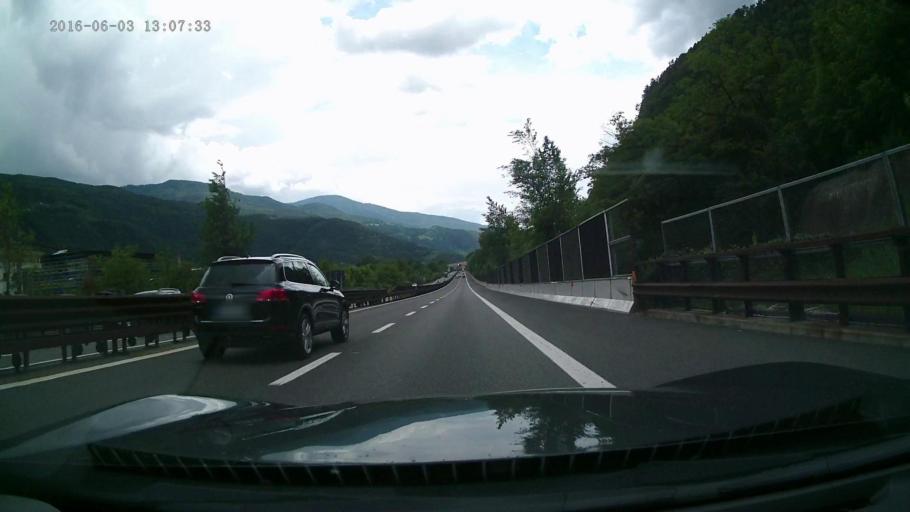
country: IT
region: Trentino-Alto Adige
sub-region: Bolzano
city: Bressanone
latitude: 46.7001
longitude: 11.6457
